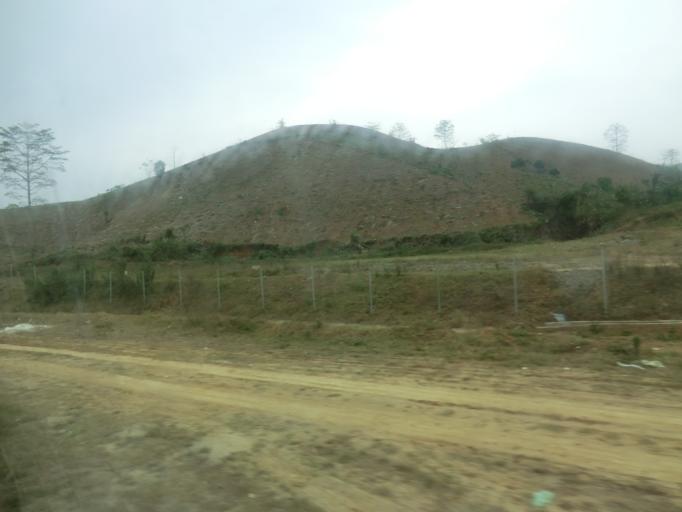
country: VN
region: Lao Cai
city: Thi Tran Khanh Yen
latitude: 22.1511
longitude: 104.3562
